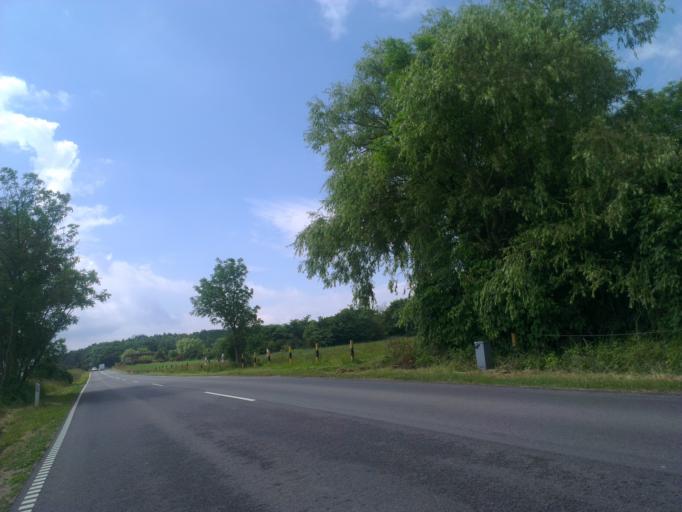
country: DK
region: Capital Region
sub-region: Frederikssund Kommune
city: Jaegerspris
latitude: 55.8811
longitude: 11.9548
